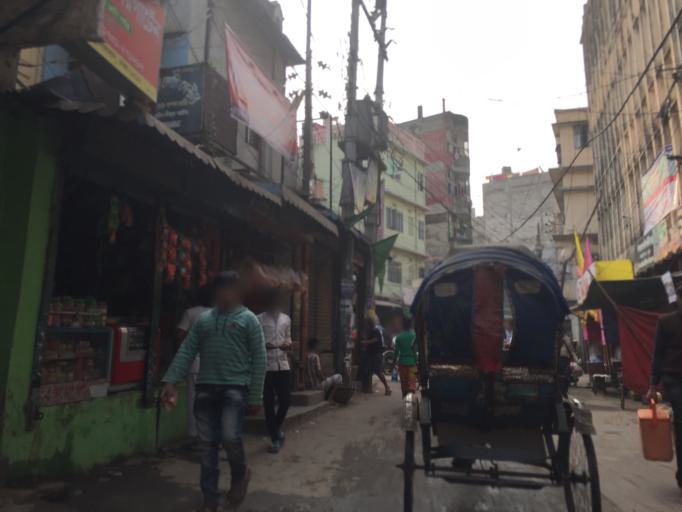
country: BD
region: Dhaka
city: Azimpur
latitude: 23.7217
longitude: 90.3796
